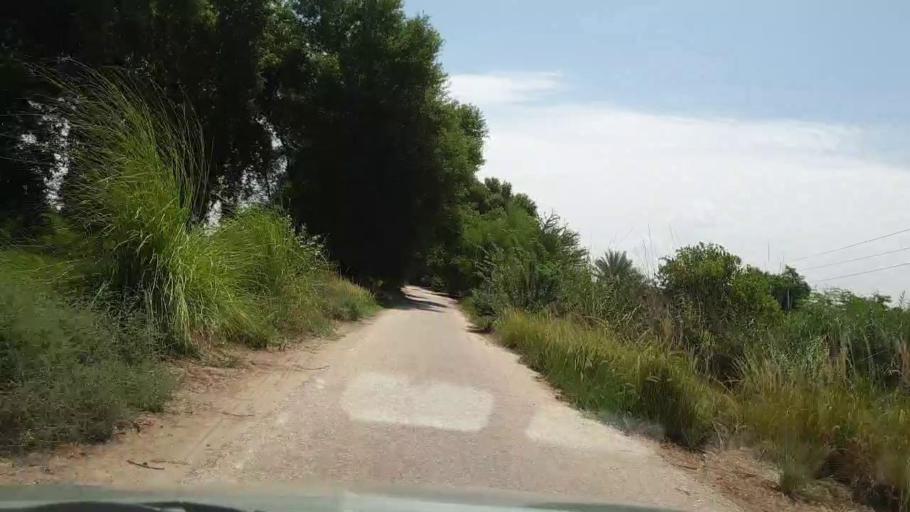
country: PK
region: Sindh
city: Bozdar
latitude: 27.0760
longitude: 68.9707
